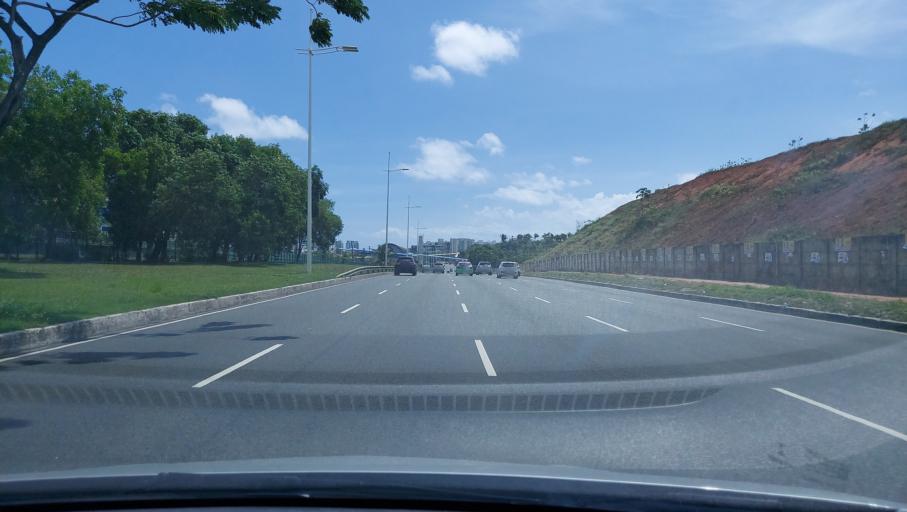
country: BR
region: Bahia
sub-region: Lauro De Freitas
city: Lauro de Freitas
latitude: -12.9309
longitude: -38.3906
